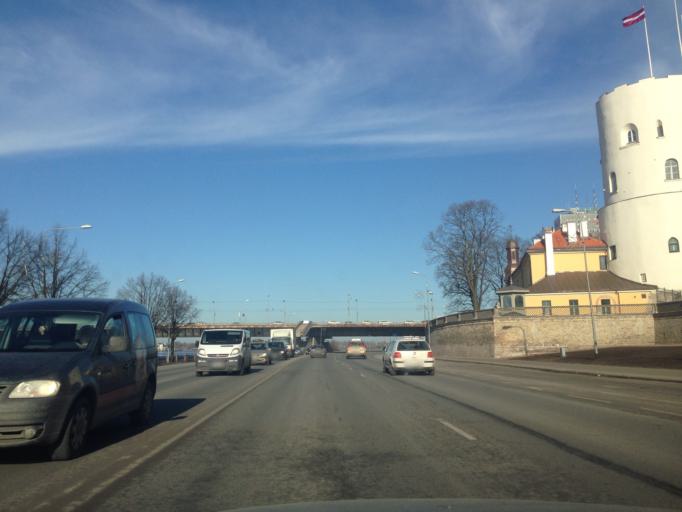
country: LV
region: Riga
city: Riga
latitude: 56.9501
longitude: 24.1002
